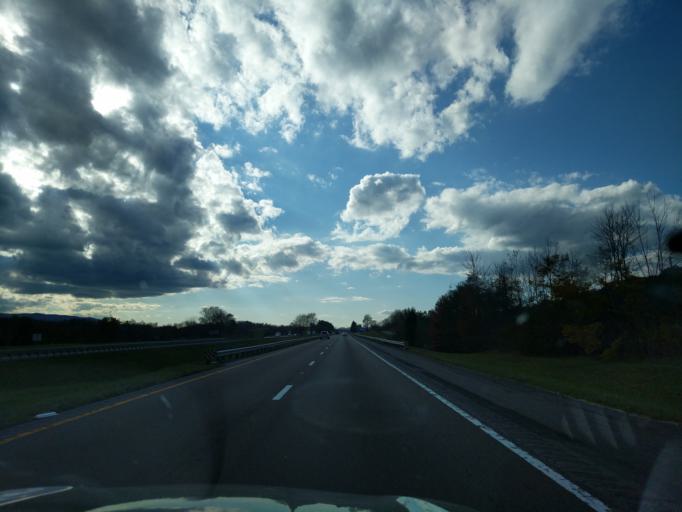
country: US
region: Virginia
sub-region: Wythe County
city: Rural Retreat
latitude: 36.9192
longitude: -81.2465
